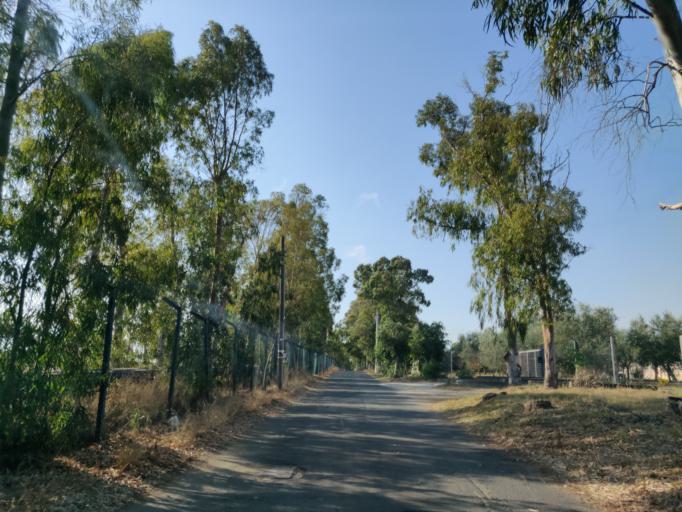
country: IT
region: Latium
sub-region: Citta metropolitana di Roma Capitale
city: Aurelia
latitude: 42.1324
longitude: 11.7646
